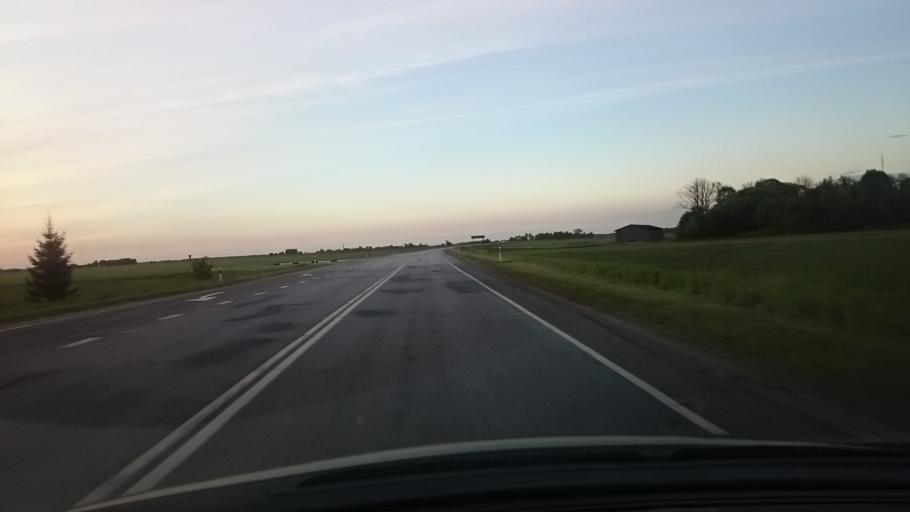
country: EE
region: Viljandimaa
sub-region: Vohma linn
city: Vohma
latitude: 58.6401
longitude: 25.5767
